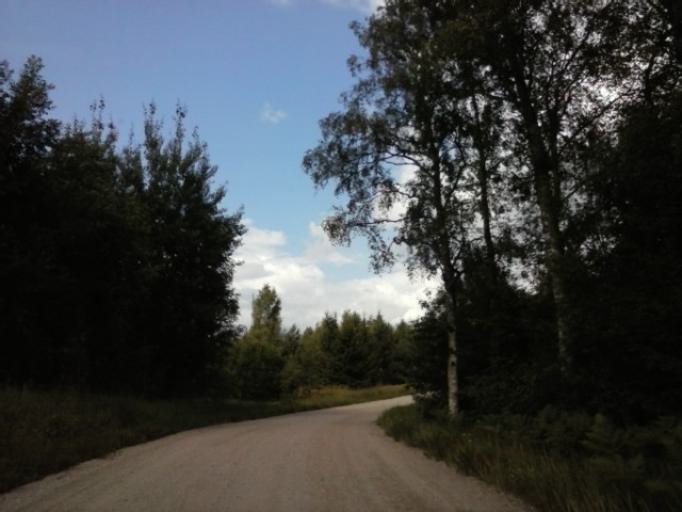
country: EE
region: Vorumaa
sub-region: Voru linn
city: Voru
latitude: 57.7661
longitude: 27.1487
